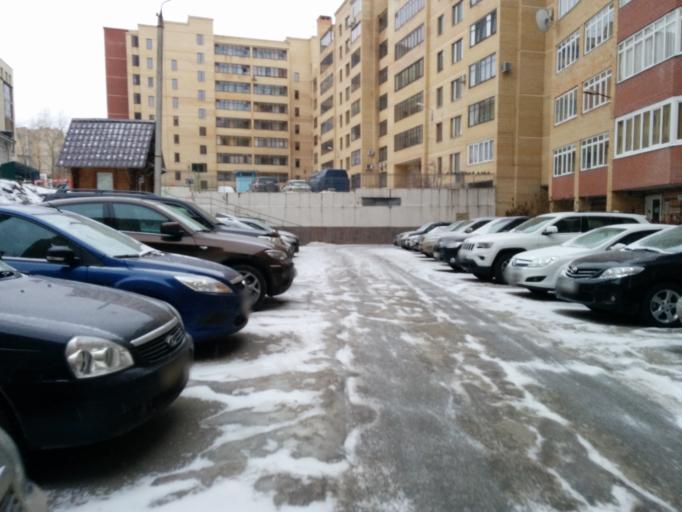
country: RU
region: Perm
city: Perm
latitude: 58.0154
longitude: 56.2598
